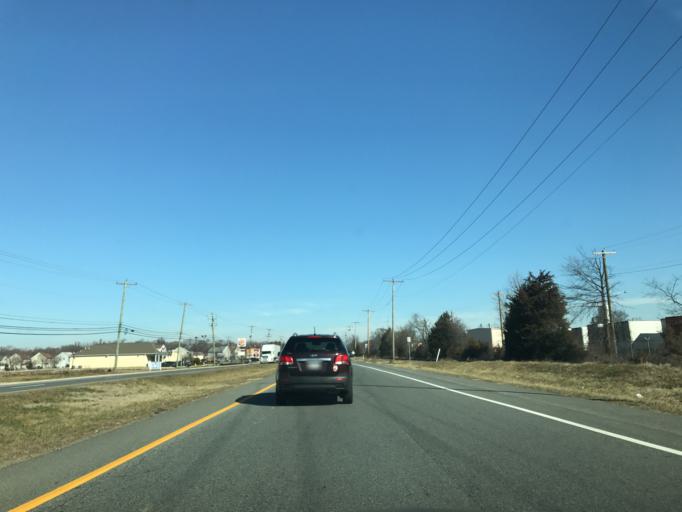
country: US
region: Delaware
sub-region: New Castle County
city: Middletown
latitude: 39.4567
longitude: -75.7227
